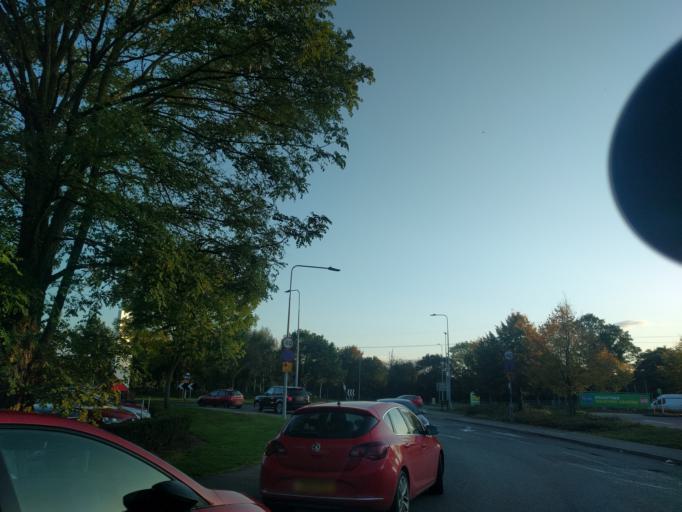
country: GB
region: England
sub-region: Essex
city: Rayne
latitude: 51.8669
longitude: 0.5809
